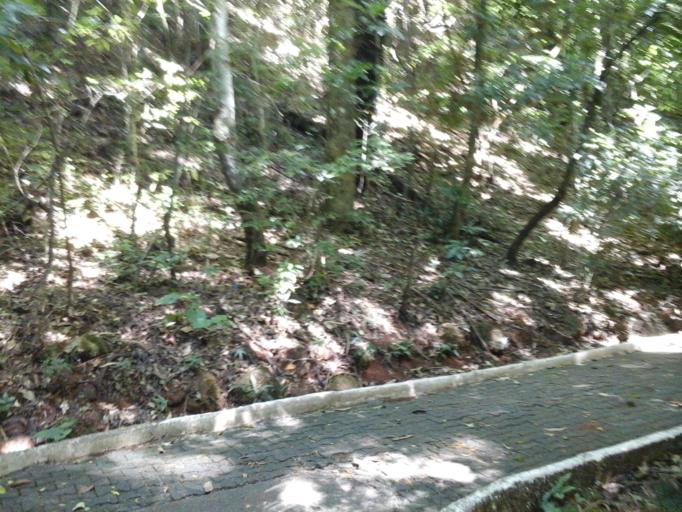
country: BR
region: Minas Gerais
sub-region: Patos De Minas
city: Patos de Minas
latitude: -18.5830
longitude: -46.5055
